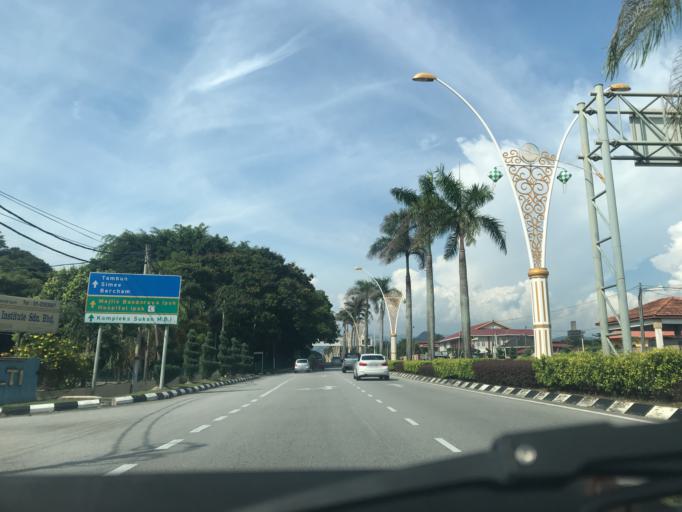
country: MY
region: Perak
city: Ipoh
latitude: 4.5929
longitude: 101.0919
